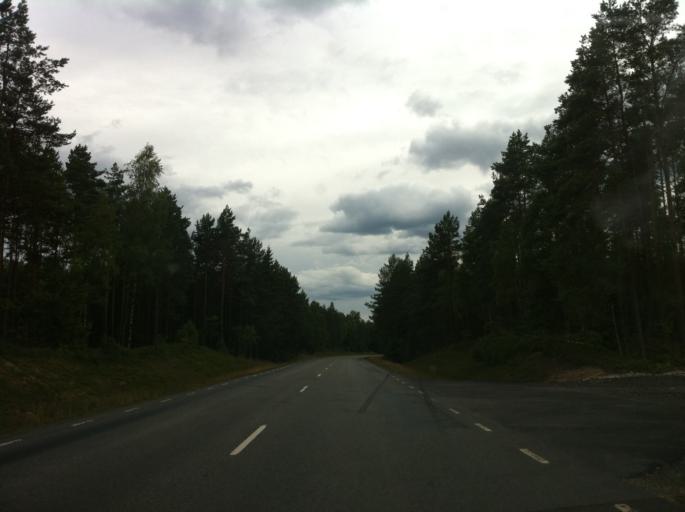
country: SE
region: Skane
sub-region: Osby Kommun
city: Lonsboda
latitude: 56.3861
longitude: 14.2746
